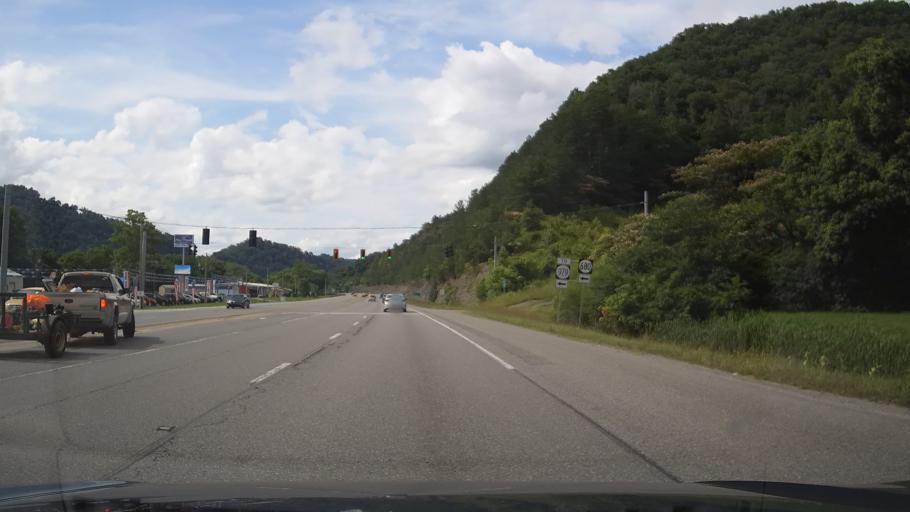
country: US
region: Kentucky
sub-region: Pike County
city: Coal Run Village
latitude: 37.5368
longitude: -82.6285
